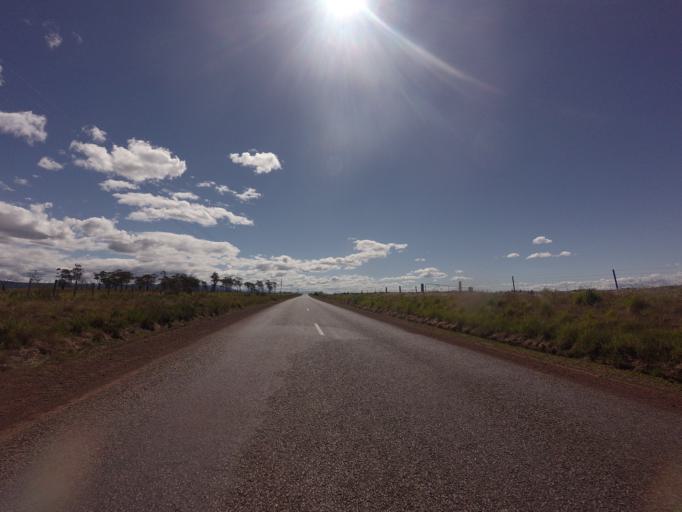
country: AU
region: Tasmania
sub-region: Northern Midlands
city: Evandale
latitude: -41.9417
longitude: 147.5169
